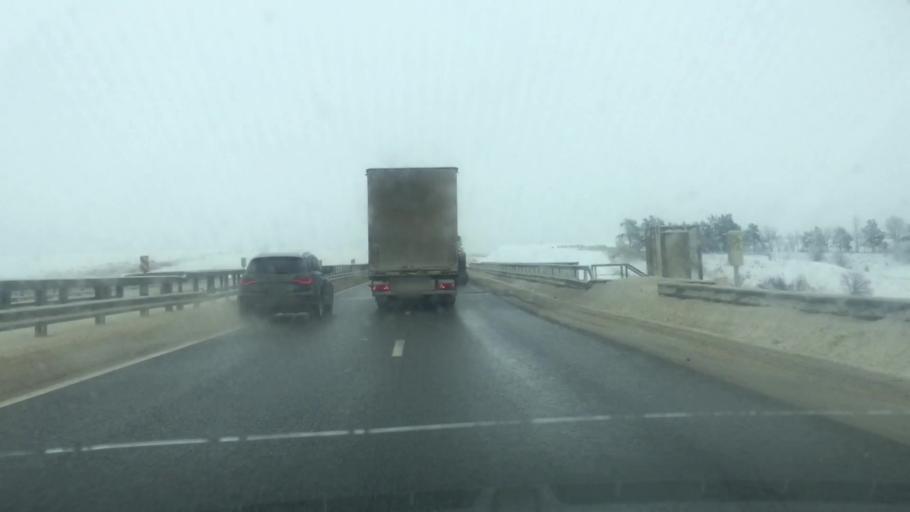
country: RU
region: Lipetsk
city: Stanovoye
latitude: 52.7896
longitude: 38.3621
